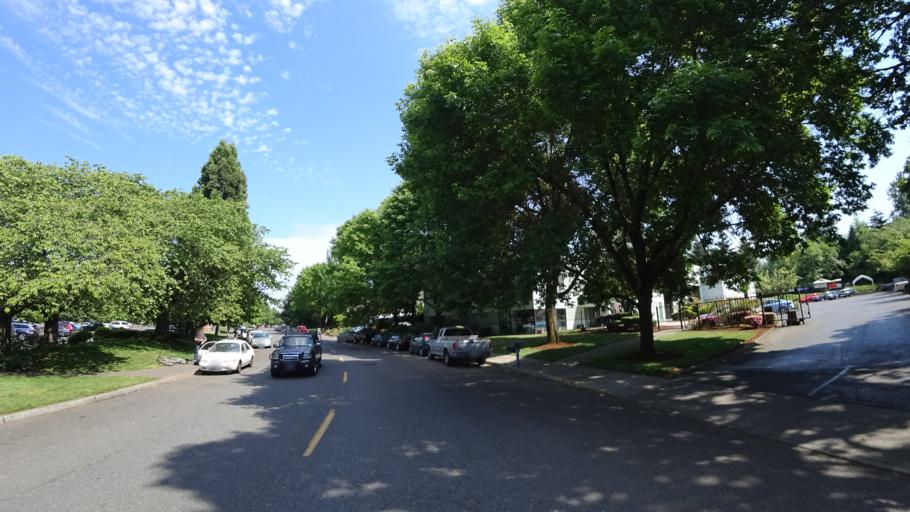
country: US
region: Oregon
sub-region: Multnomah County
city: Lents
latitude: 45.5657
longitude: -122.5420
